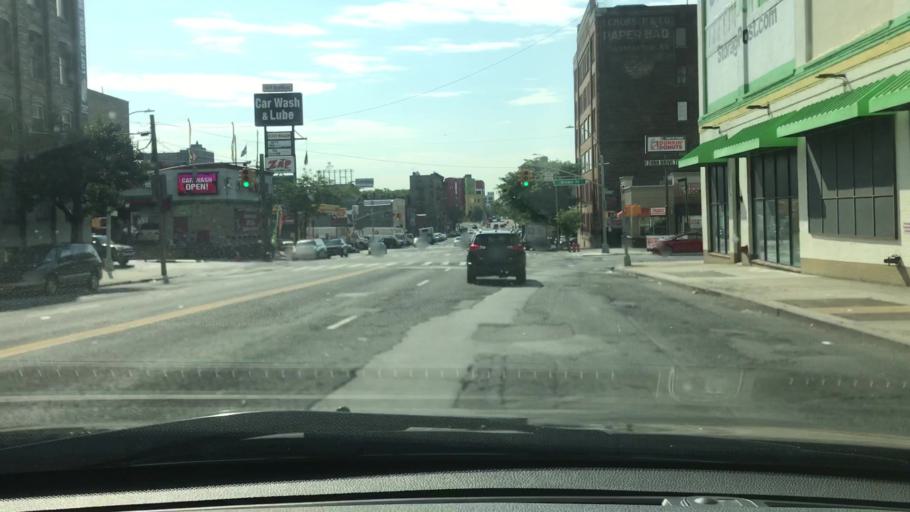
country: US
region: New York
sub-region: New York County
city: Manhattan
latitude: 40.8049
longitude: -73.9230
